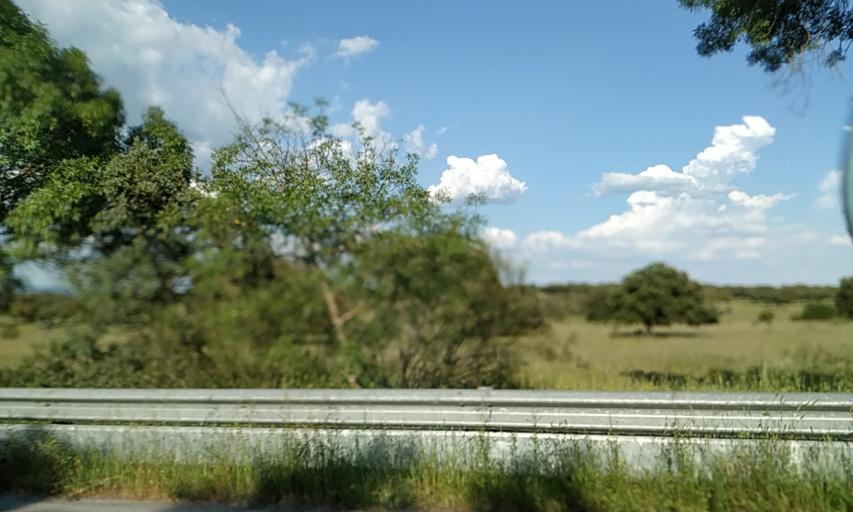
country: PT
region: Portalegre
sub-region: Portalegre
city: Urra
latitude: 39.1579
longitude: -7.4542
